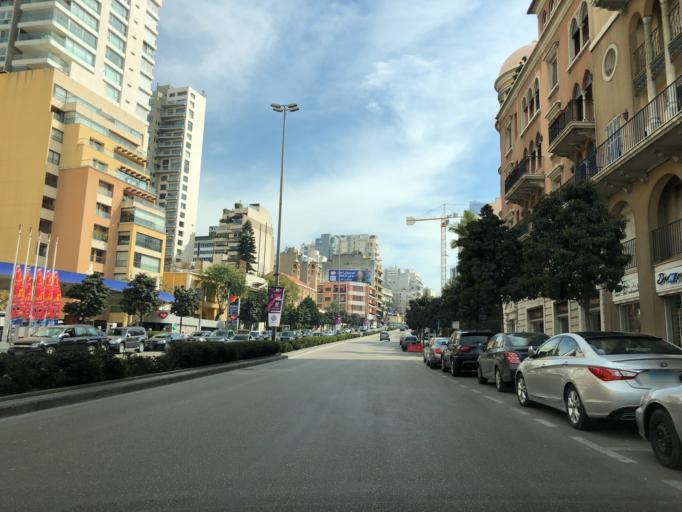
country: LB
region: Beyrouth
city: Beirut
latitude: 33.8948
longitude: 35.5092
